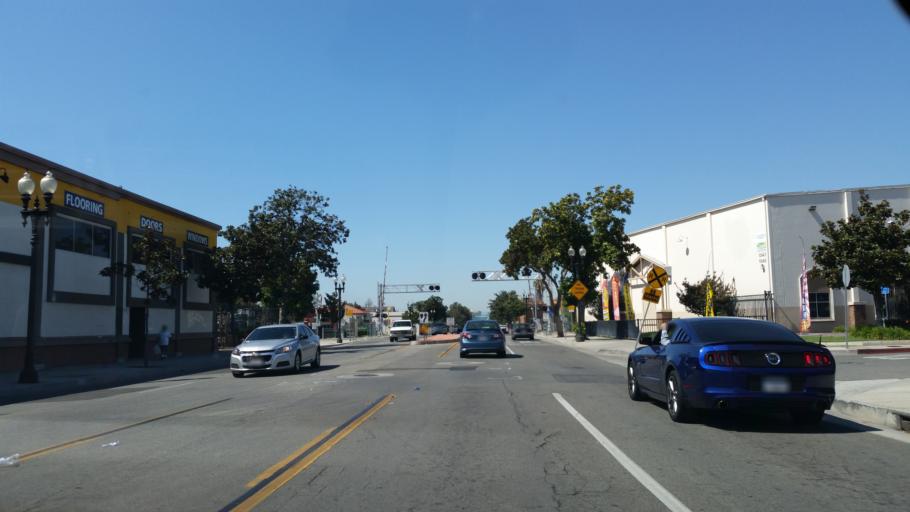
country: US
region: California
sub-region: Orange County
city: Santa Ana
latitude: 33.7481
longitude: -117.8547
